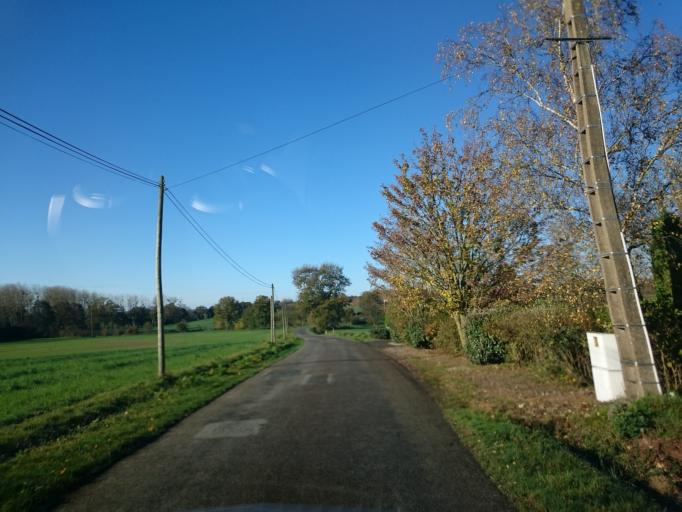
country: FR
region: Brittany
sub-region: Departement d'Ille-et-Vilaine
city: Corps-Nuds
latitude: 47.9517
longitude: -1.5549
